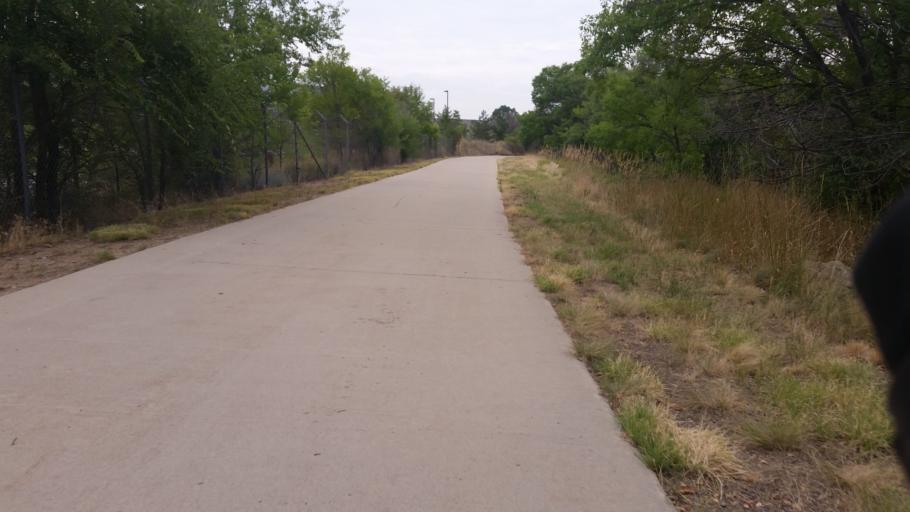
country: US
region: Colorado
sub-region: Adams County
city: Welby
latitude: 39.8285
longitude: -104.9579
